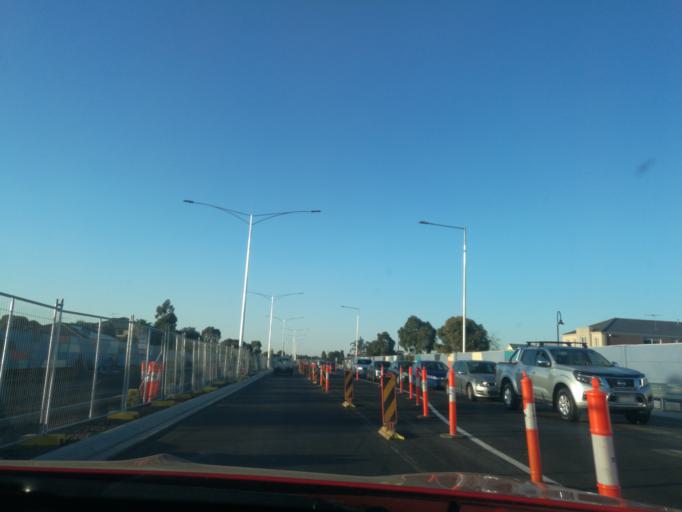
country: AU
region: Victoria
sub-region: Wyndham
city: Williams Landing
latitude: -37.8814
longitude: 144.7477
